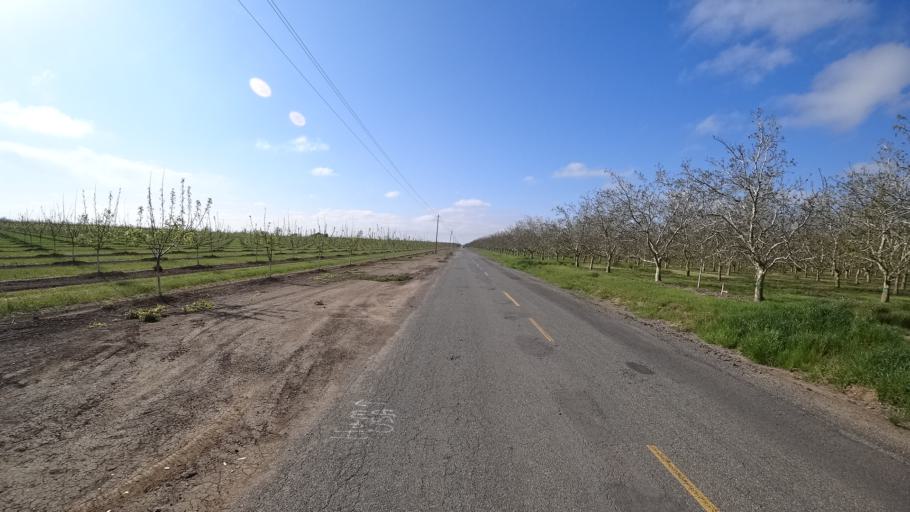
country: US
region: California
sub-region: Glenn County
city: Willows
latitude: 39.4770
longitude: -121.9677
